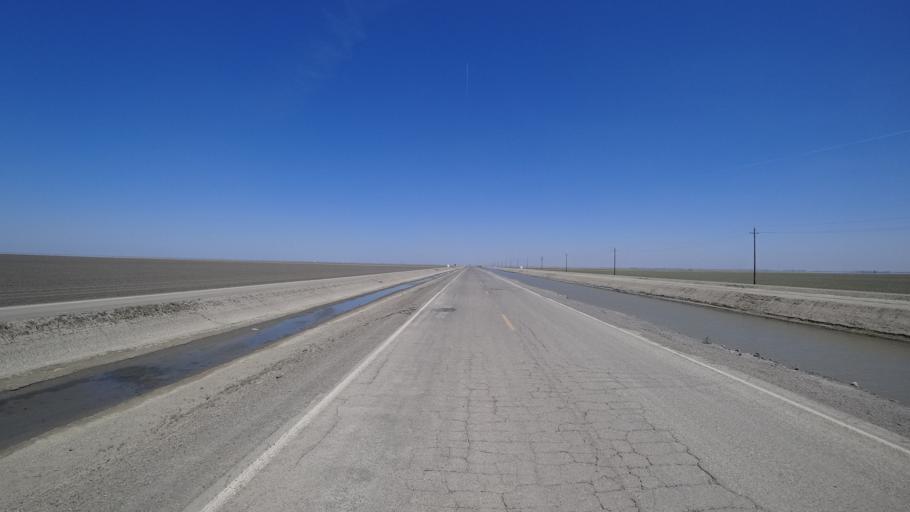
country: US
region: California
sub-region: Kings County
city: Corcoran
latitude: 36.0100
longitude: -119.6432
